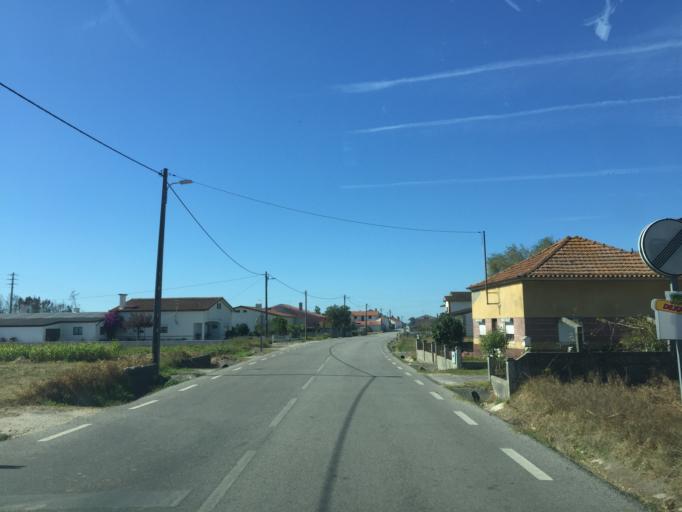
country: PT
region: Coimbra
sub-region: Mira
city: Mira
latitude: 40.3183
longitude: -8.7643
